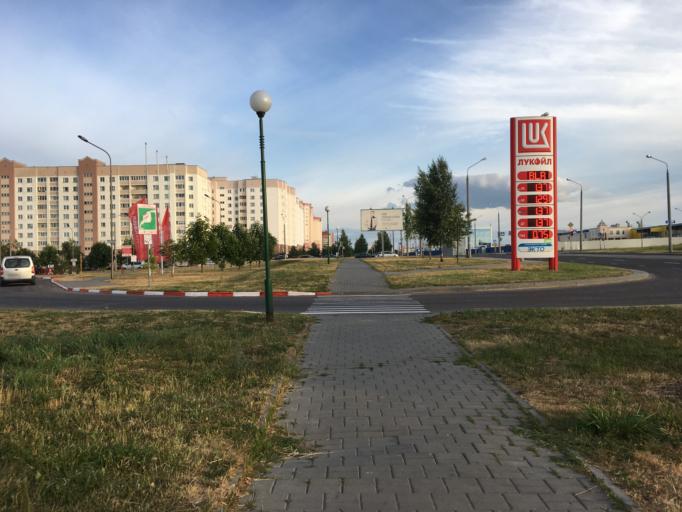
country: BY
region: Grodnenskaya
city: Hrodna
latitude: 53.7173
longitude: 23.8403
